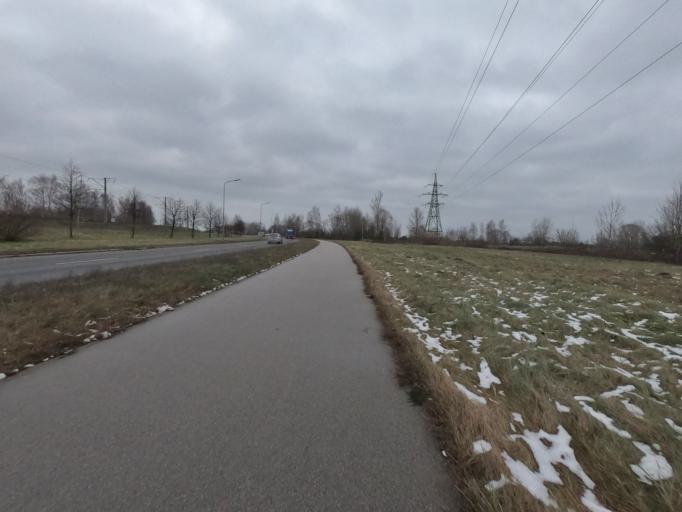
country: LV
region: Riga
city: Jaunciems
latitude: 57.0267
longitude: 24.1391
